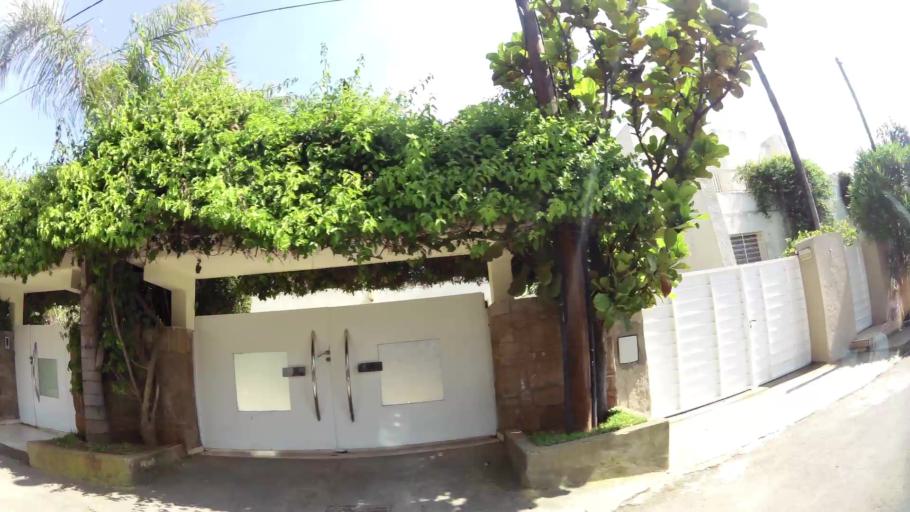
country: MA
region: Rabat-Sale-Zemmour-Zaer
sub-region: Rabat
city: Rabat
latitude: 33.9852
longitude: -6.8315
